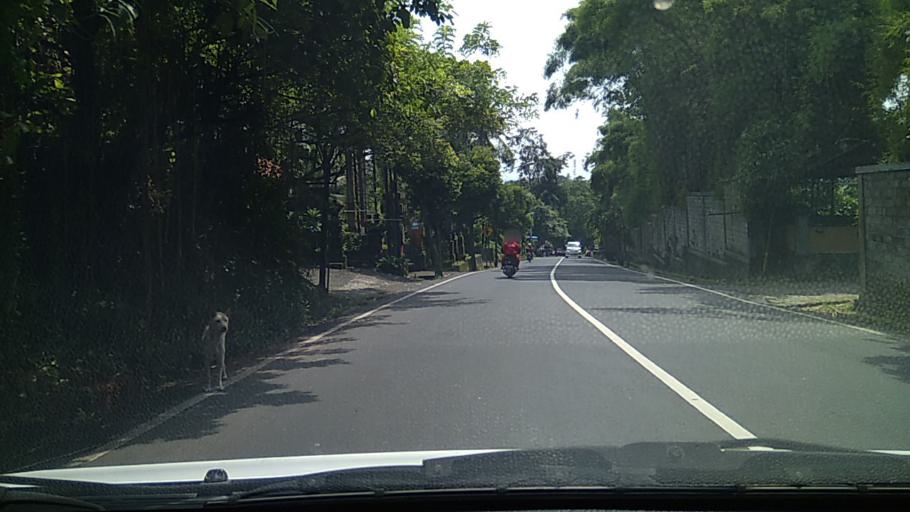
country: ID
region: Bali
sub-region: Kabupaten Gianyar
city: Ubud
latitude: -8.5227
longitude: 115.2817
